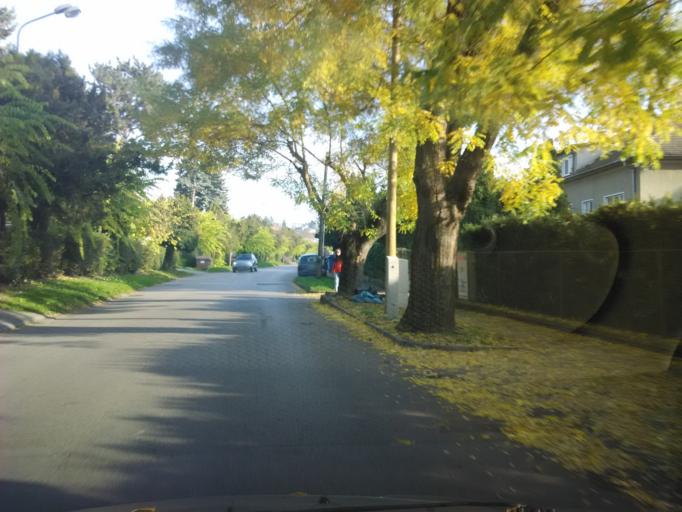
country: SK
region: Nitriansky
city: Levice
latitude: 48.2204
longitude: 18.6137
